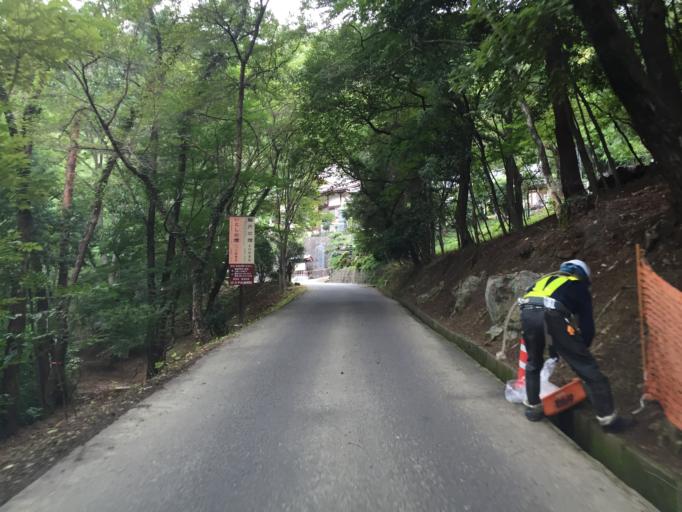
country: JP
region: Fukushima
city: Fukushima-shi
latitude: 37.7714
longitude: 140.4725
